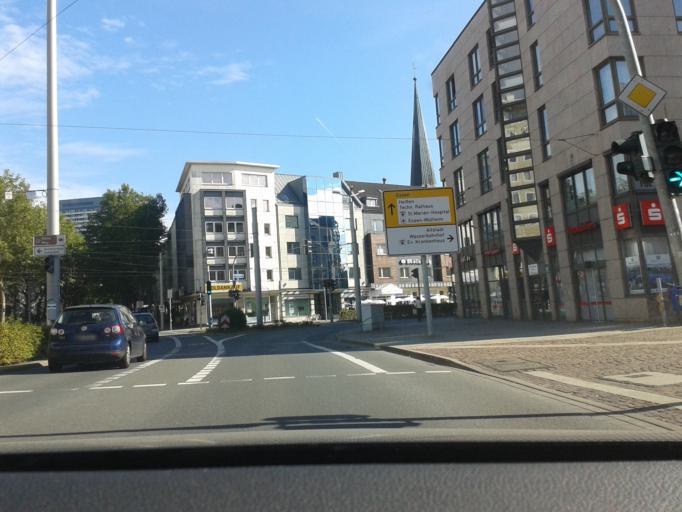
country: DE
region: North Rhine-Westphalia
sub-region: Regierungsbezirk Dusseldorf
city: Muelheim (Ruhr)
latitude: 51.4266
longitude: 6.8799
